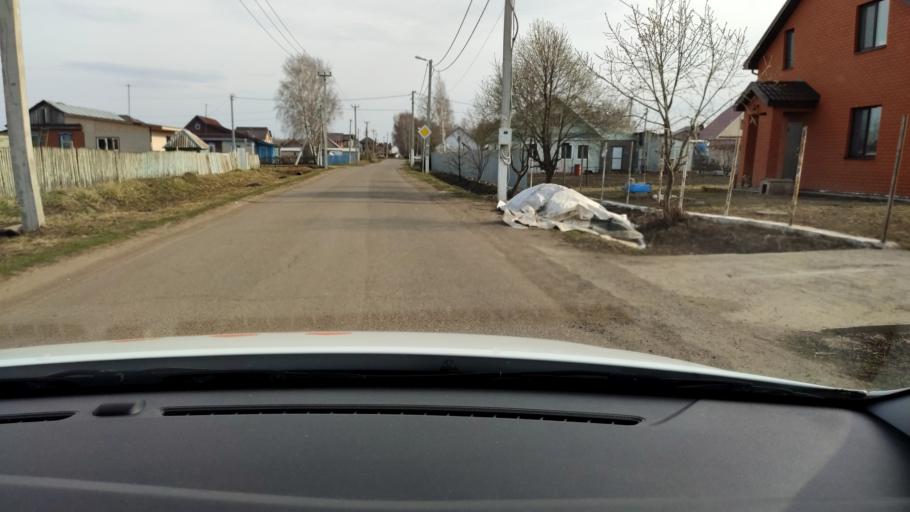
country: RU
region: Tatarstan
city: Stolbishchi
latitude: 55.6464
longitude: 49.3107
